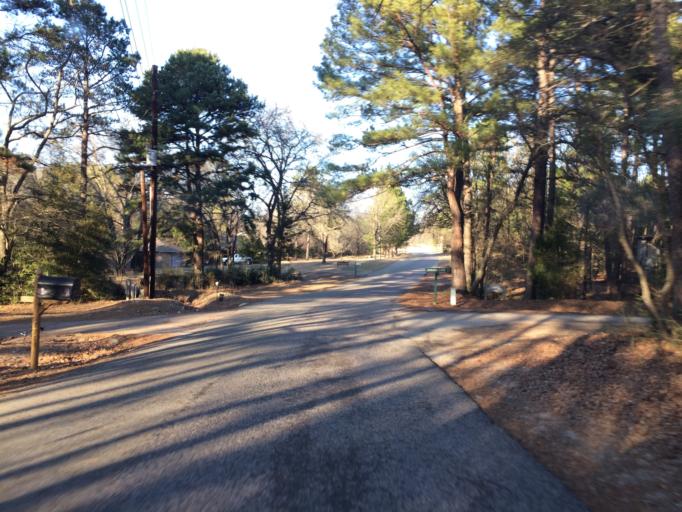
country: US
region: Texas
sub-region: Wood County
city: Hawkins
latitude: 32.7170
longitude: -95.1796
